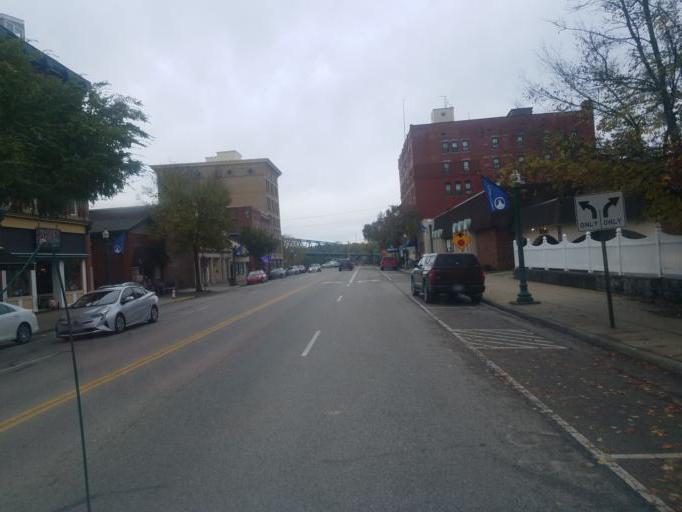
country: US
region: Ohio
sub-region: Washington County
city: Marietta
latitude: 39.4115
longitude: -81.4530
